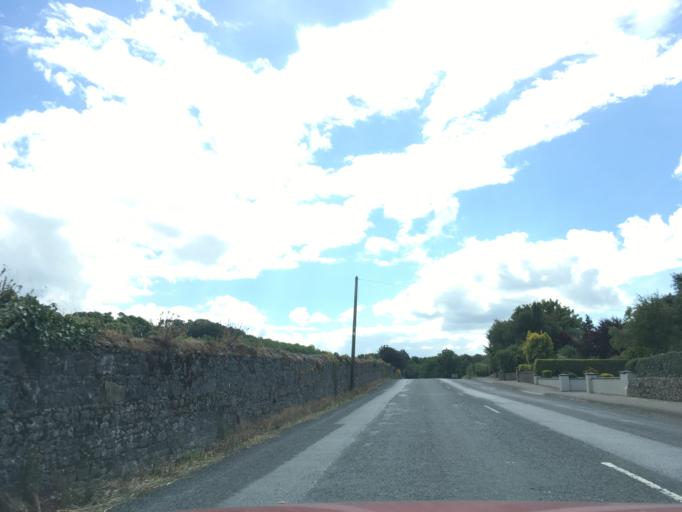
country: IE
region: Munster
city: Cahir
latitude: 52.3686
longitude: -7.9322
